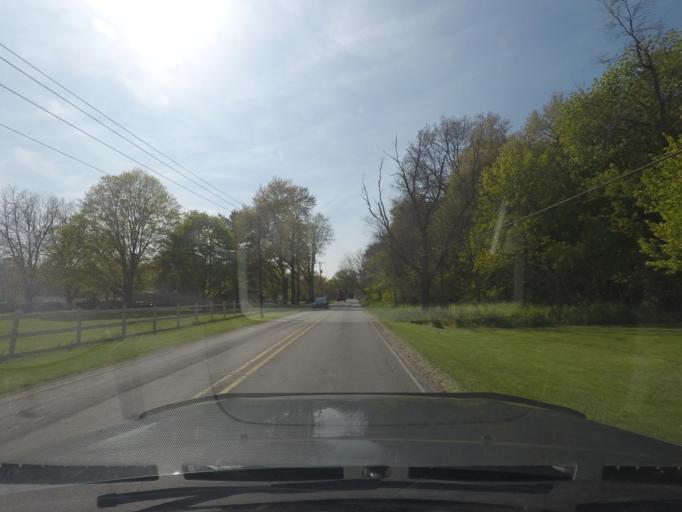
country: US
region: Indiana
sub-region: Elkhart County
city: Elkhart
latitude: 41.7054
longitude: -86.0138
